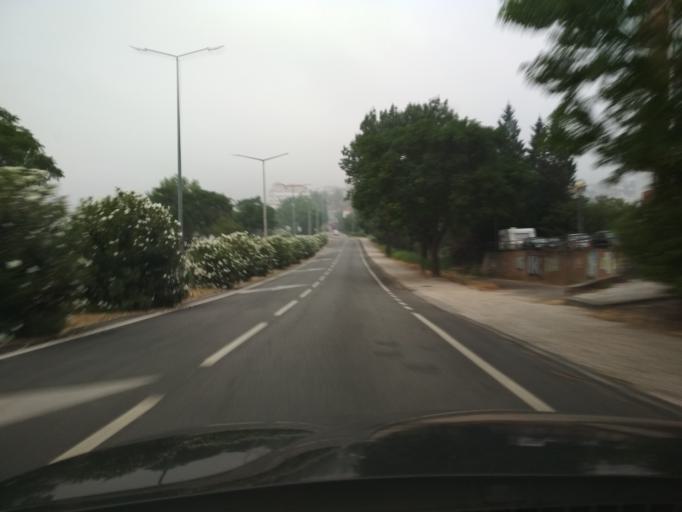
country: PT
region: Coimbra
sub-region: Coimbra
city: Coimbra
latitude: 40.1961
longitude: -8.4208
